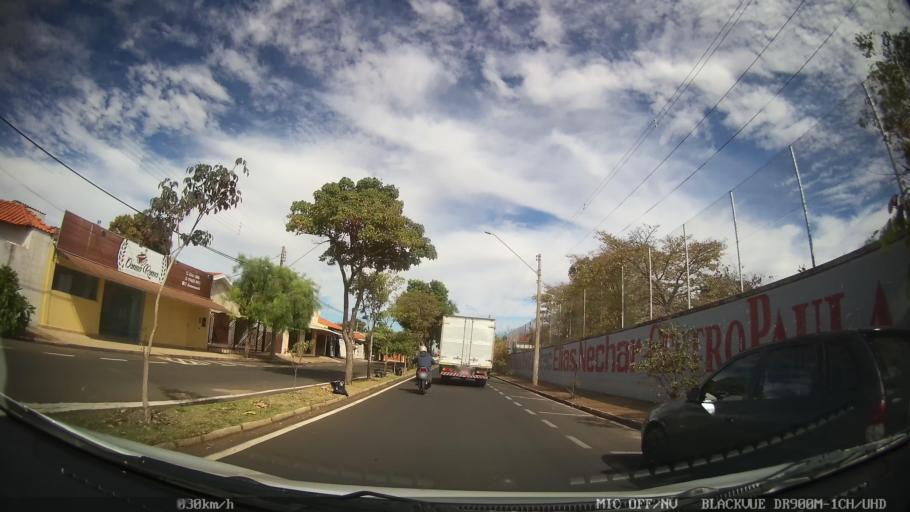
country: BR
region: Sao Paulo
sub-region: Catanduva
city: Catanduva
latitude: -21.1308
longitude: -48.9557
